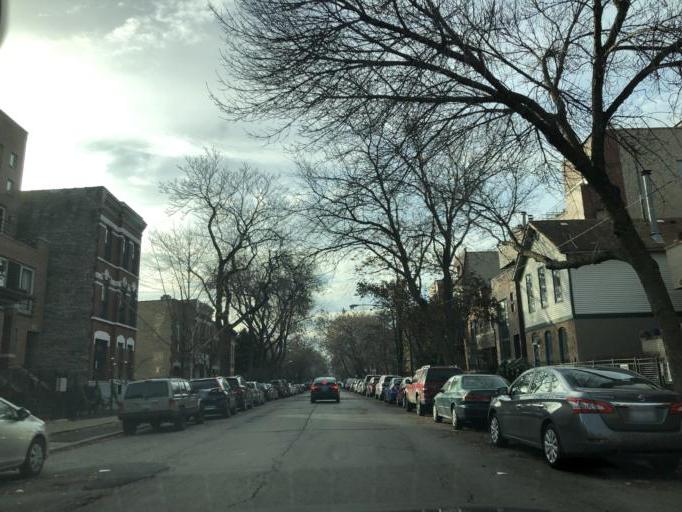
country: US
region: Illinois
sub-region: Cook County
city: Chicago
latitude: 41.9014
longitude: -87.6748
